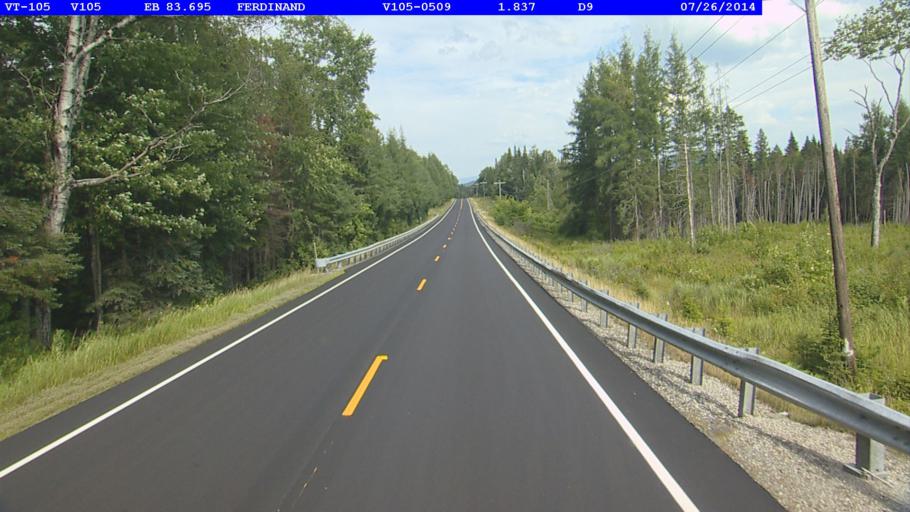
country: US
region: New Hampshire
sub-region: Coos County
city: Stratford
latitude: 44.7802
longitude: -71.7682
